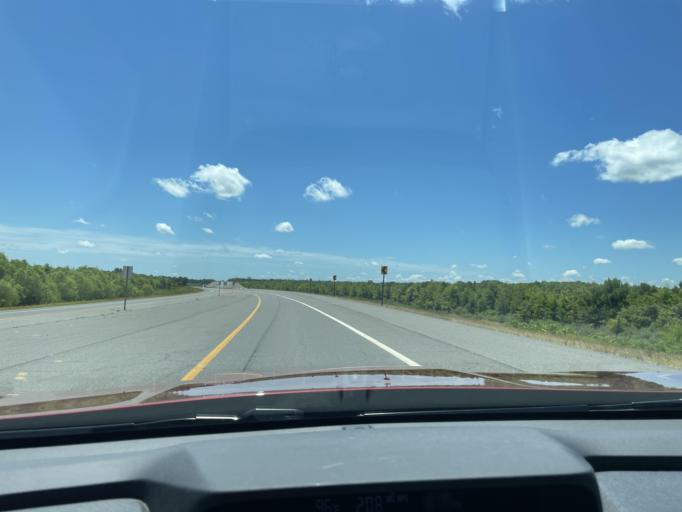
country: US
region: Arkansas
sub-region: Jefferson County
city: Pine Bluff
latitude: 34.1644
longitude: -91.9852
